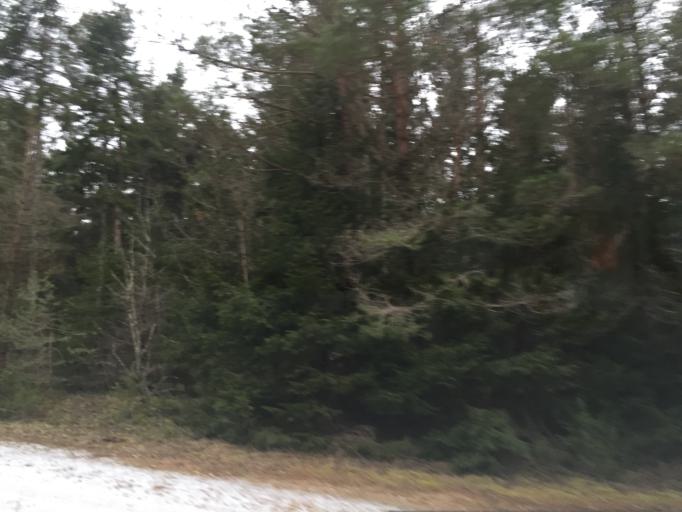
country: EE
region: Saare
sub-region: Kuressaare linn
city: Kuressaare
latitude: 58.4072
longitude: 22.1995
